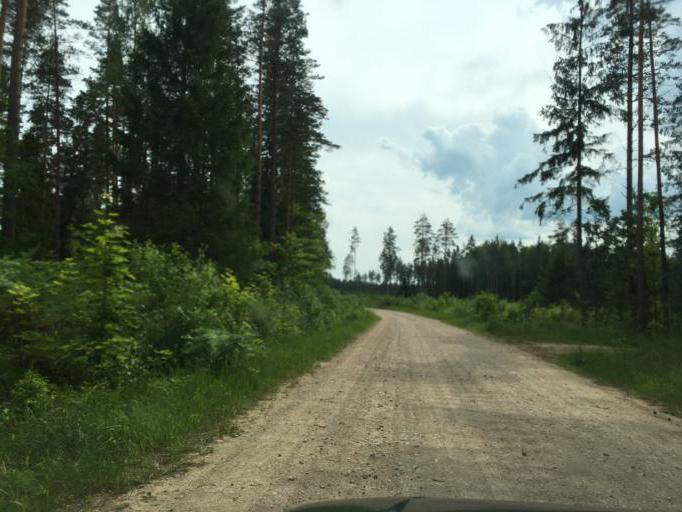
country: LV
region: Rugaju
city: Rugaji
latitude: 56.7758
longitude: 27.1046
